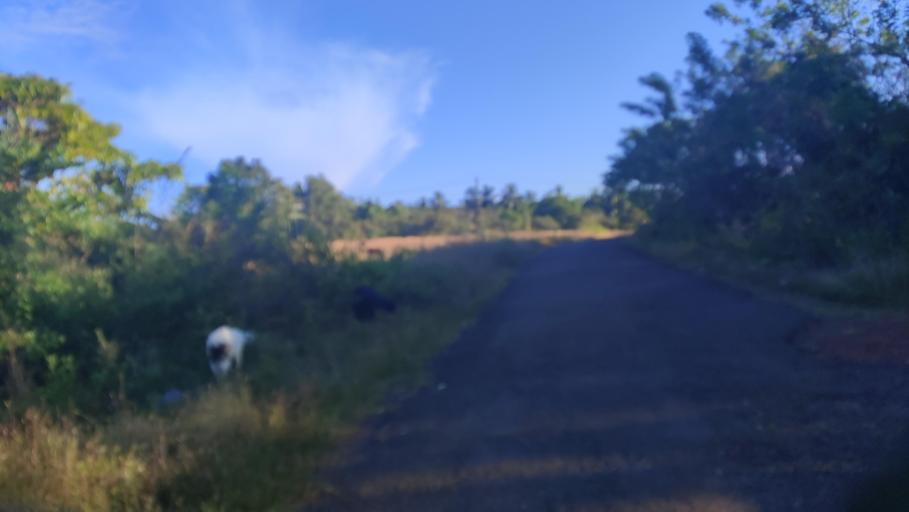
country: IN
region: Kerala
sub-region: Kasaragod District
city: Kasaragod
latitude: 12.4984
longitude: 75.0810
